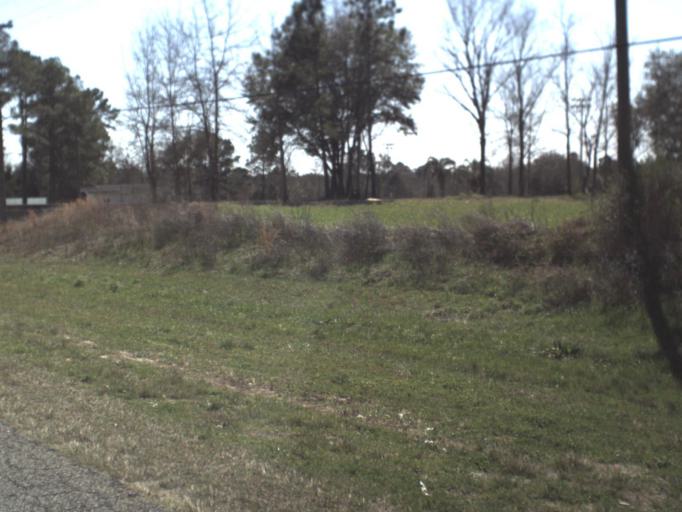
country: US
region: Florida
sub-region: Jackson County
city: Graceville
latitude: 30.9423
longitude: -85.3928
